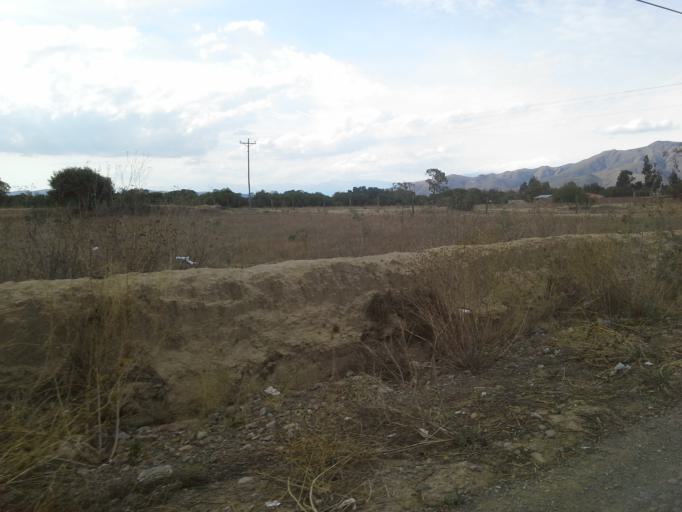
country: BO
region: Cochabamba
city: Tarata
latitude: -17.5879
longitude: -66.0183
